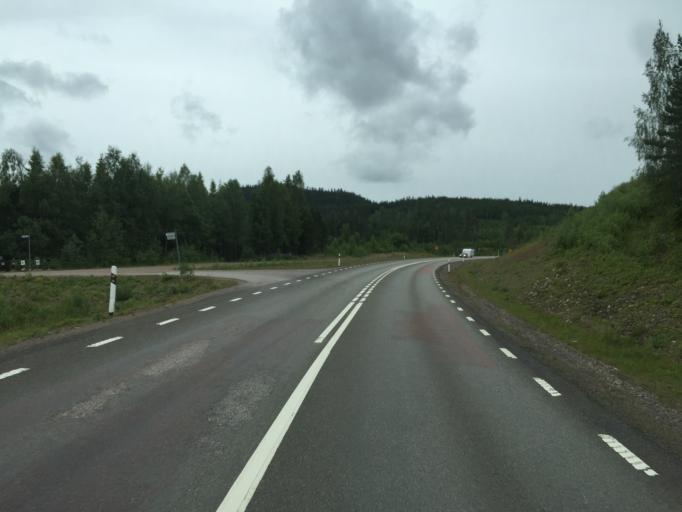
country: SE
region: Dalarna
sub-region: Malung-Saelens kommun
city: Malung
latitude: 60.6149
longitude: 13.6071
